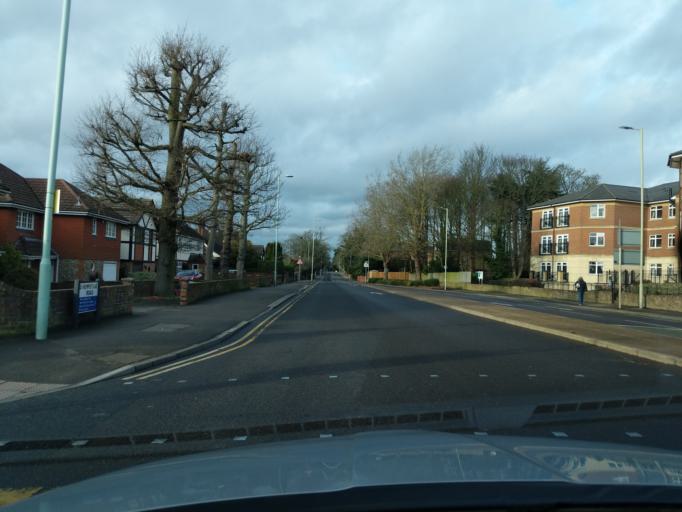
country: GB
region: England
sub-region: Hertfordshire
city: Watford
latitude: 51.6631
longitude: -0.4084
